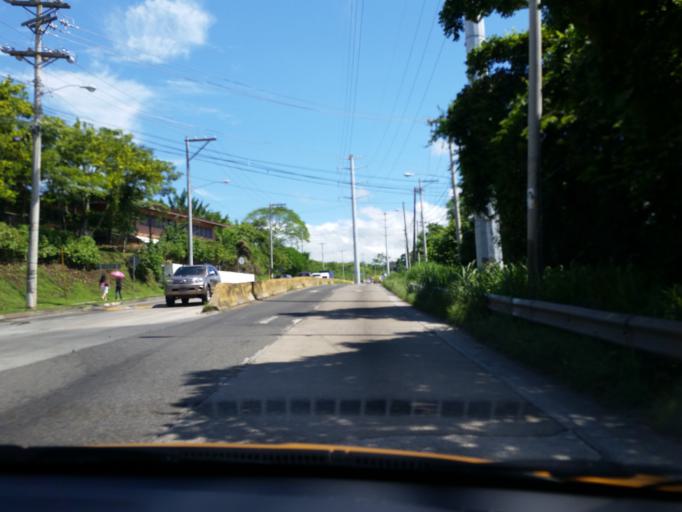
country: PA
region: Panama
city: San Miguelito
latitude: 9.0602
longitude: -79.4621
